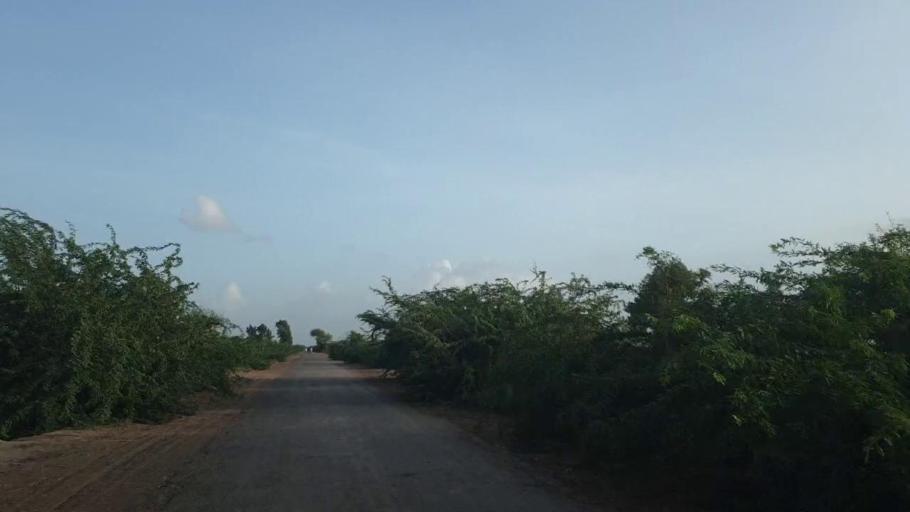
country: PK
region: Sindh
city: Kadhan
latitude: 24.6111
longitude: 69.1158
